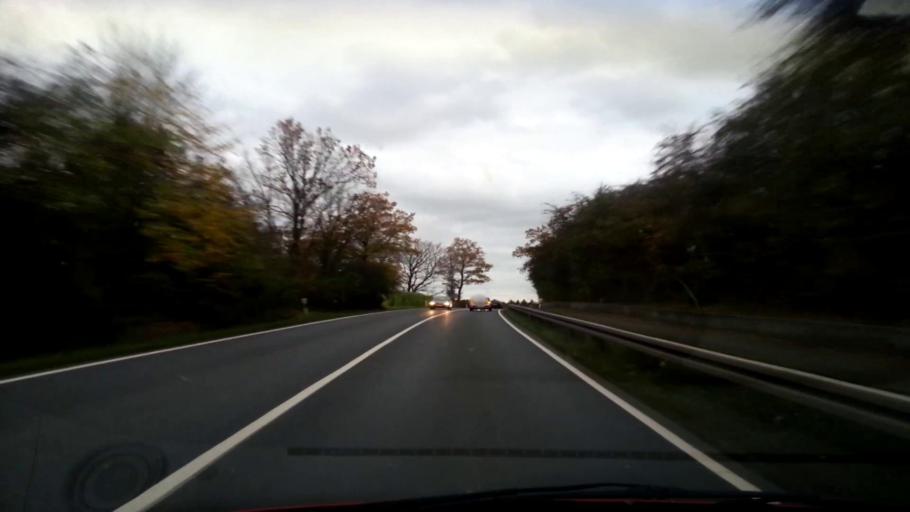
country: DE
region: Bavaria
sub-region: Upper Franconia
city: Sonnefeld
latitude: 50.2166
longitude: 11.1016
